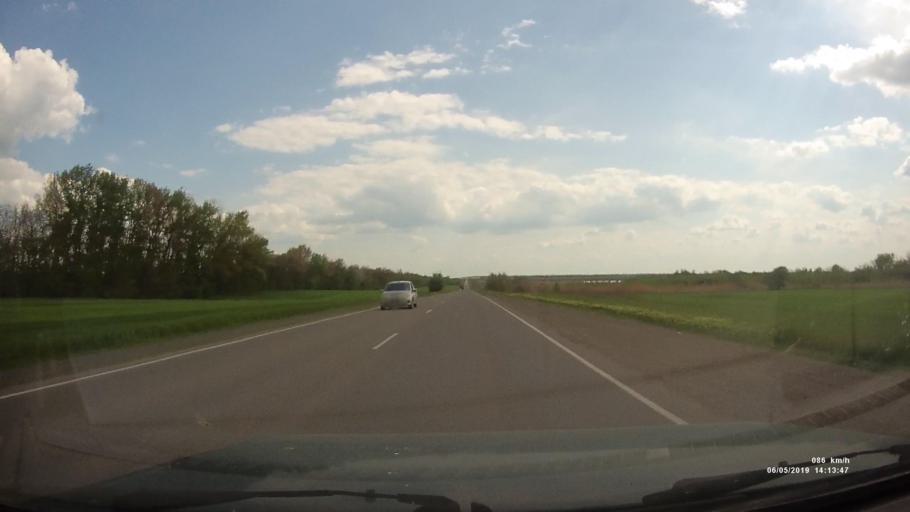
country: RU
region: Rostov
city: Kamenolomni
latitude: 47.6566
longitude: 40.2949
